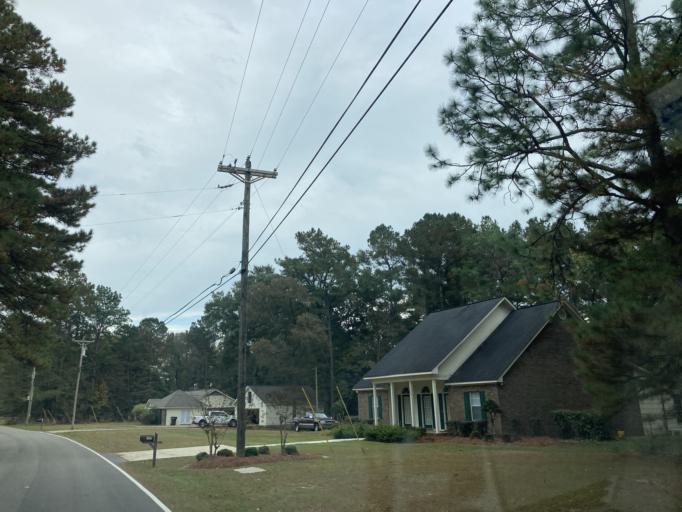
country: US
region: Mississippi
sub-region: Lamar County
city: West Hattiesburg
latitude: 31.2968
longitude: -89.4308
